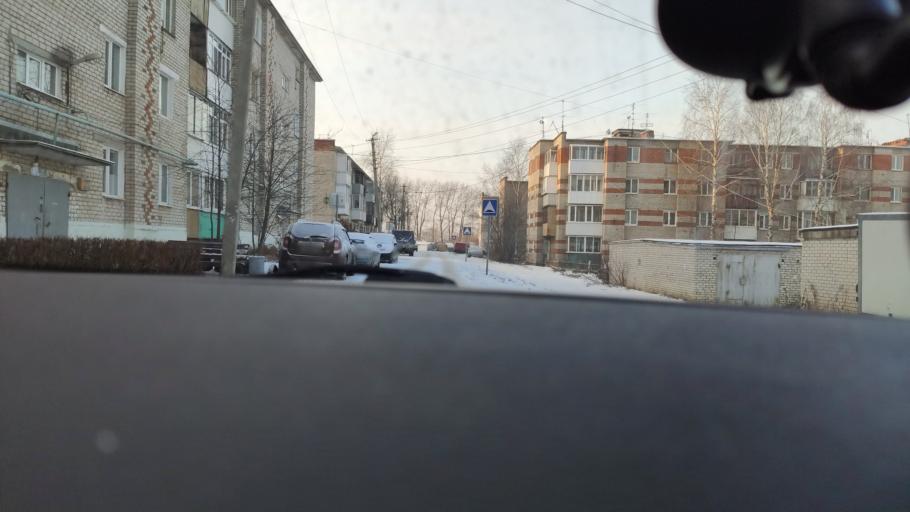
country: RU
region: Perm
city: Kondratovo
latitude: 57.9455
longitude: 56.0650
